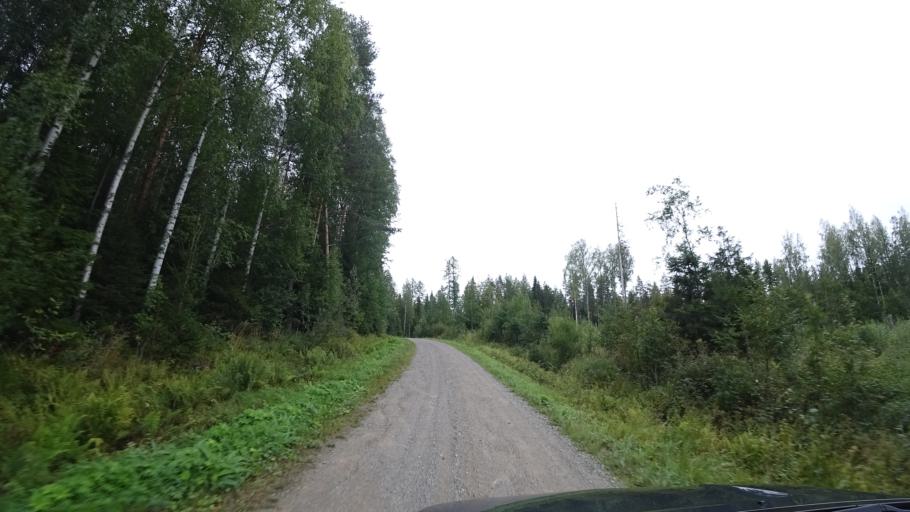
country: FI
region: Paijanne Tavastia
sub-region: Lahti
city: Auttoinen
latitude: 61.2206
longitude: 25.1471
